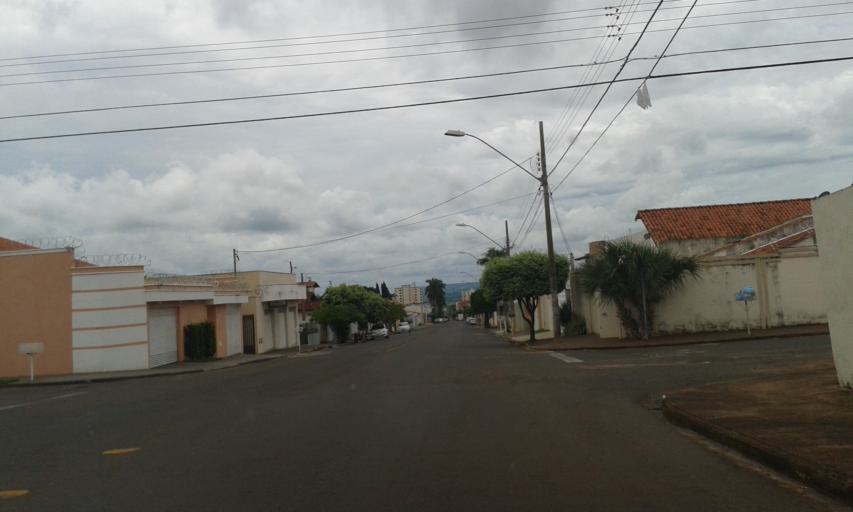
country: BR
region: Minas Gerais
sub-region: Ituiutaba
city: Ituiutaba
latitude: -18.9860
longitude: -49.4593
